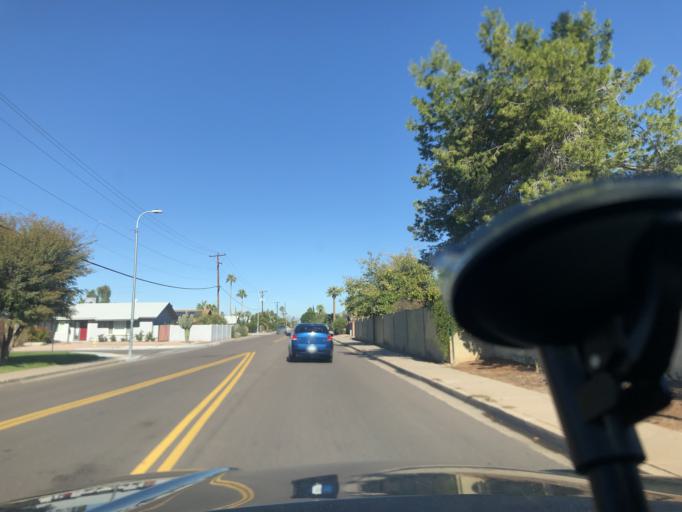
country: US
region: Arizona
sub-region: Maricopa County
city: Scottsdale
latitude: 33.5098
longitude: -111.8959
